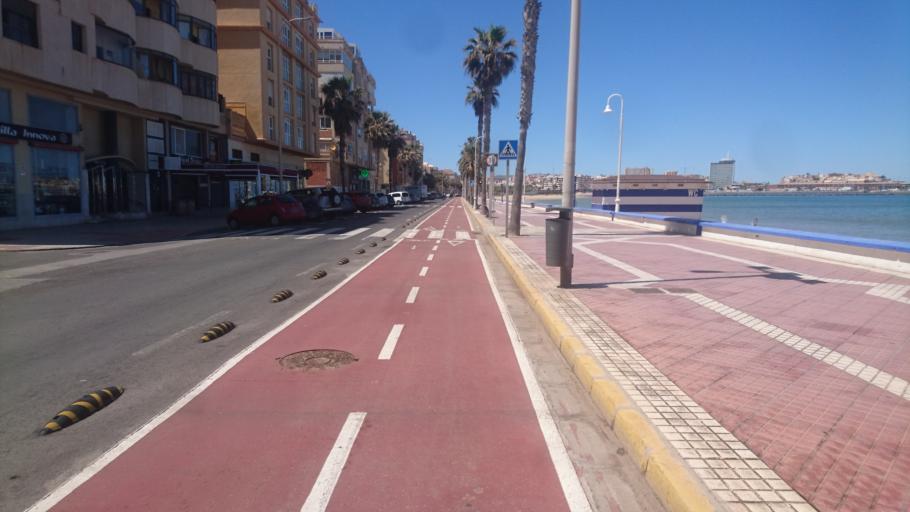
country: ES
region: Melilla
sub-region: Melilla
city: Melilla
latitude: 35.2792
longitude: -2.9362
